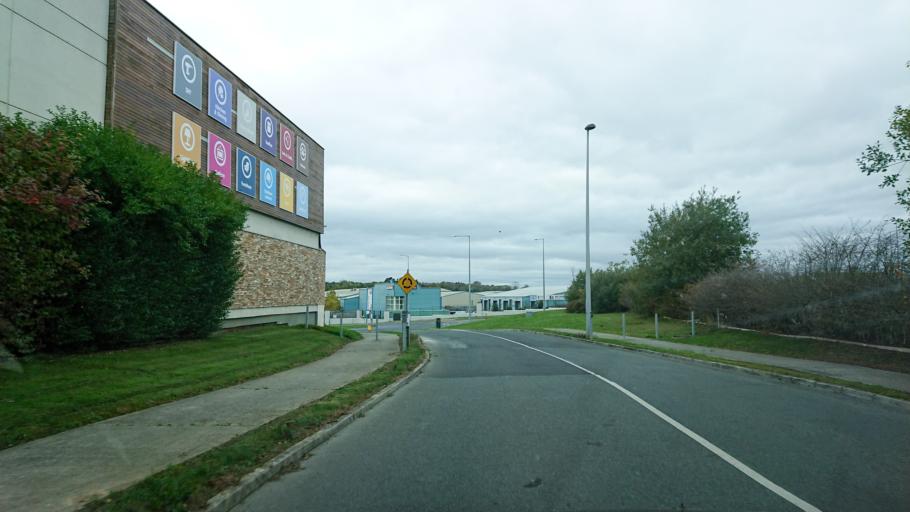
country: IE
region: Munster
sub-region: Waterford
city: Waterford
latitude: 52.2324
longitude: -7.1409
